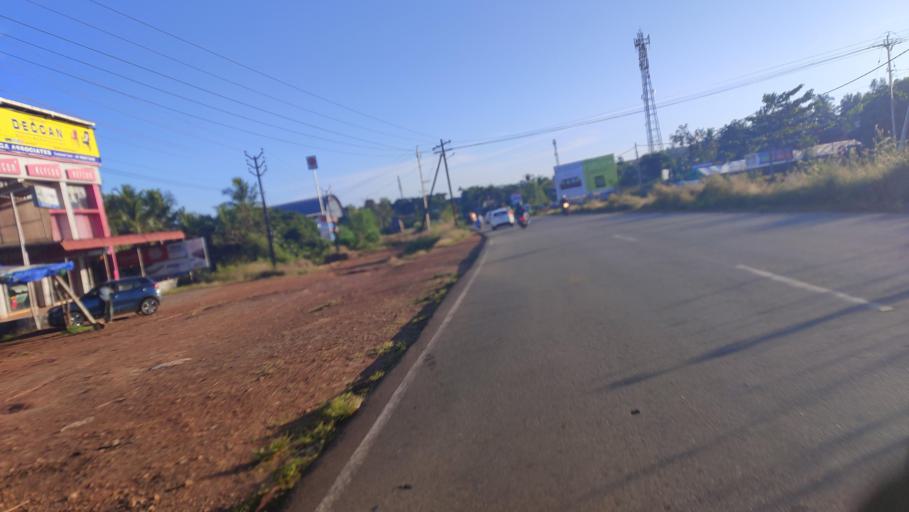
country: IN
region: Kerala
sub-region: Kasaragod District
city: Kasaragod
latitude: 12.4698
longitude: 75.0578
